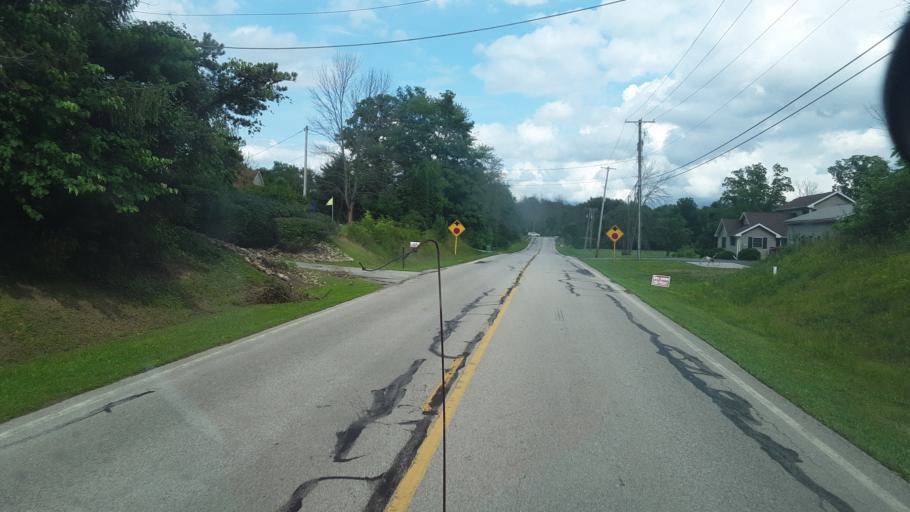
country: US
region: Ohio
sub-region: Ashtabula County
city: Jefferson
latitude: 41.7826
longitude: -80.7679
